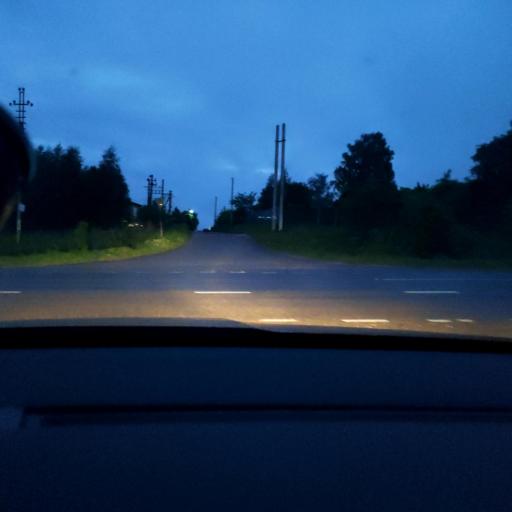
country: RU
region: Moskovskaya
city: Dmitrov
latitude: 56.3272
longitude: 37.5831
